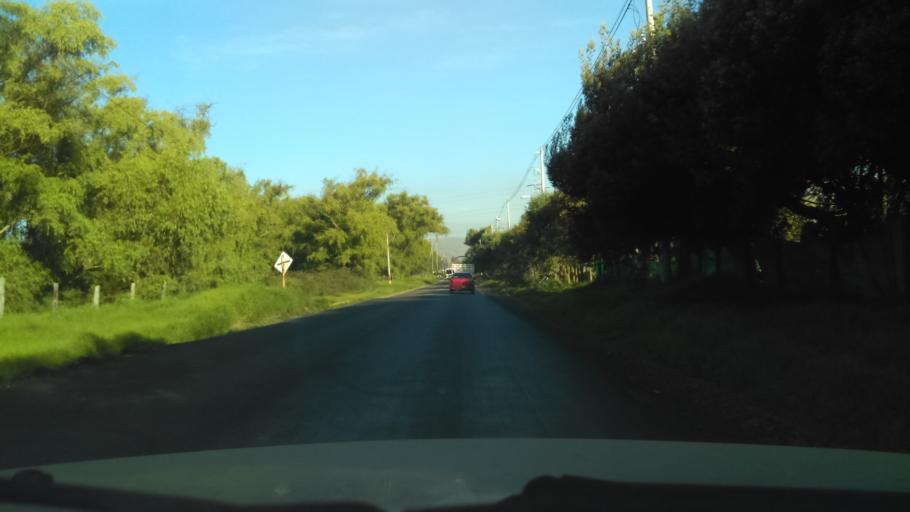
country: CO
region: Cundinamarca
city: Sibate
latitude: 4.5323
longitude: -74.2410
